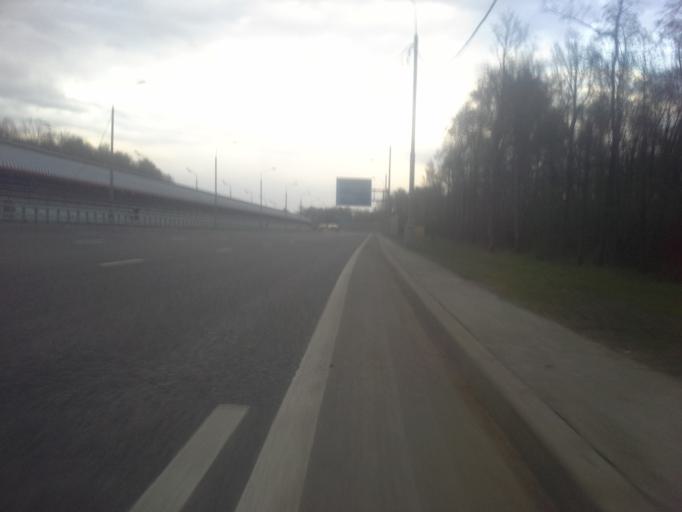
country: RU
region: Moskovskaya
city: Mosrentgen
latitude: 55.5796
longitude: 37.4464
